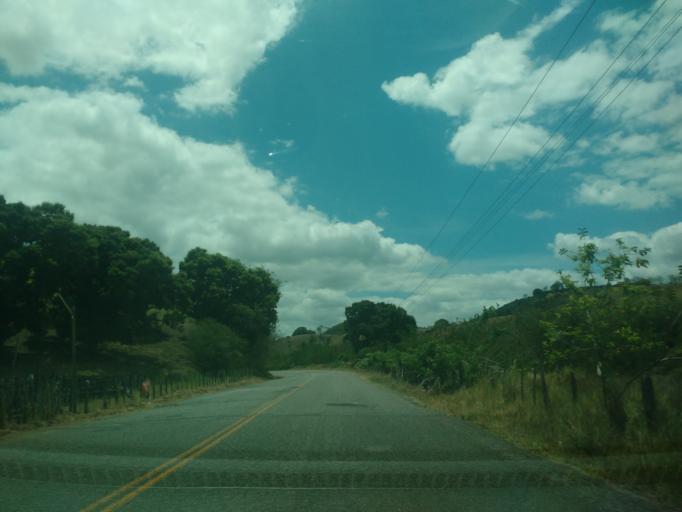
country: BR
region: Alagoas
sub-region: Santana Do Mundau
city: Santana do Mundau
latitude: -9.1452
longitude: -36.1696
